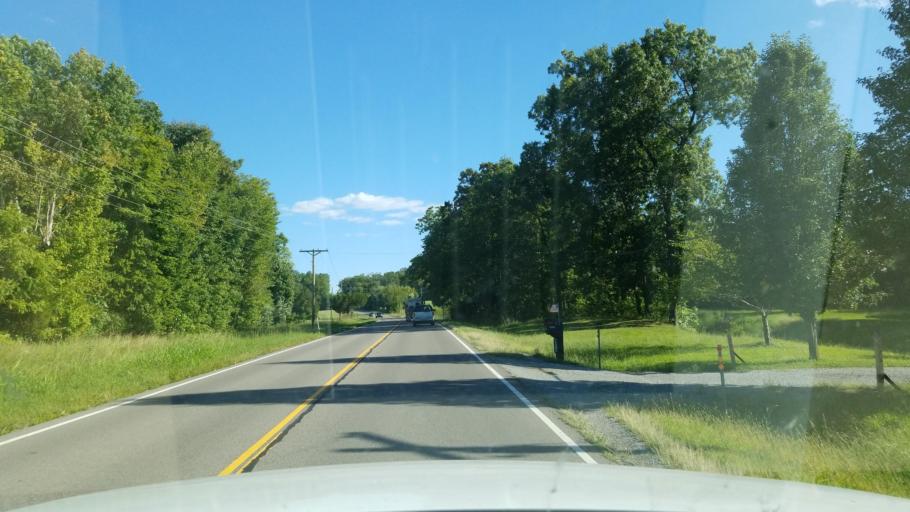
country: US
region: Illinois
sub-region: Saline County
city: Harrisburg
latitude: 37.6266
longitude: -88.4753
